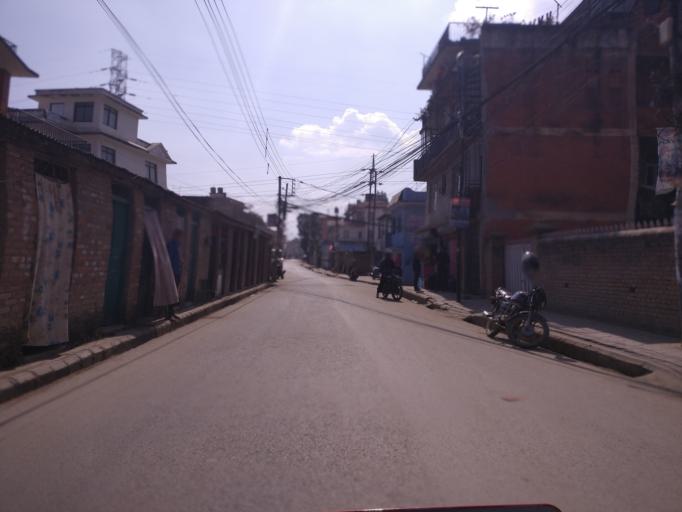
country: NP
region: Central Region
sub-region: Bagmati Zone
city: Patan
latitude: 27.6665
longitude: 85.3138
